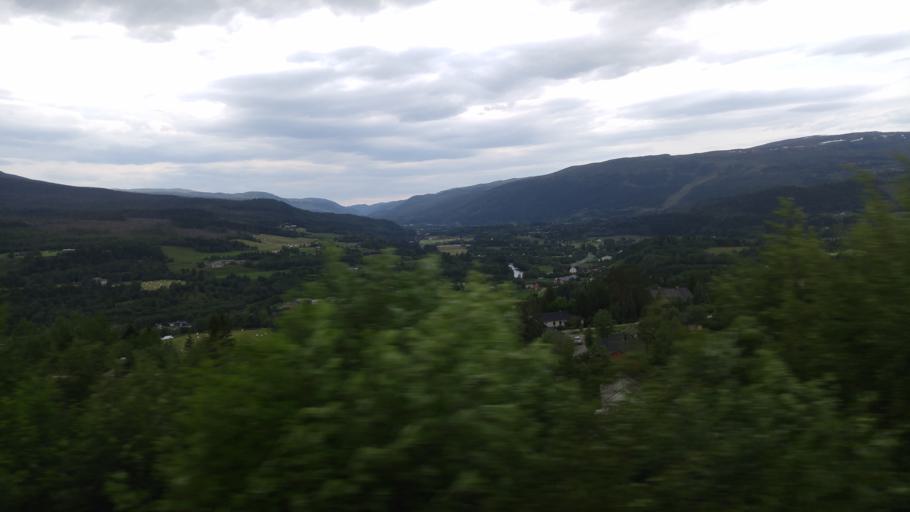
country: NO
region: Nord-Trondelag
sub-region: Meraker
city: Meraker
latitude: 63.4182
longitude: 11.7542
